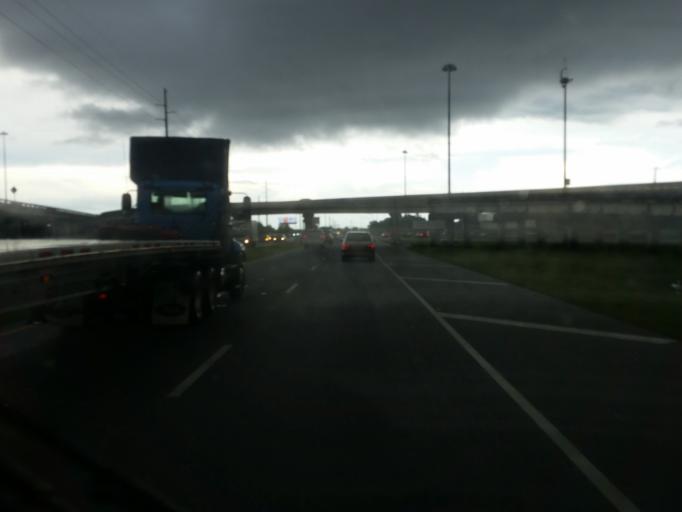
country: US
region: Alabama
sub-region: Mobile County
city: Mobile
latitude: 30.6916
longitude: -88.0269
